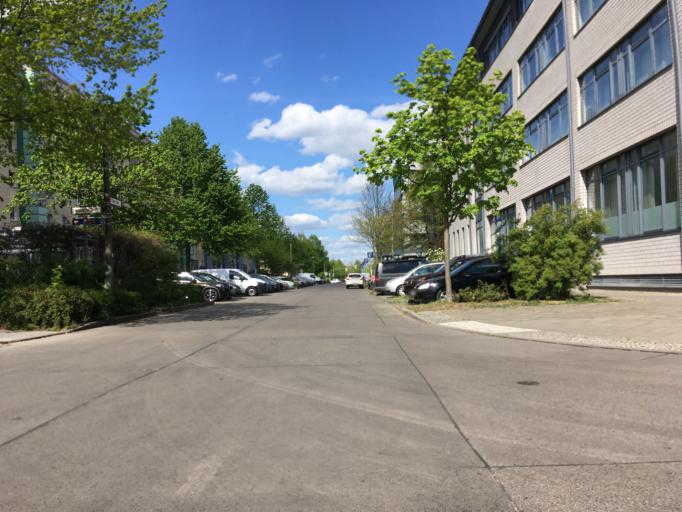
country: DE
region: Berlin
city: Hellersdorf
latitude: 52.5301
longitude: 13.6145
